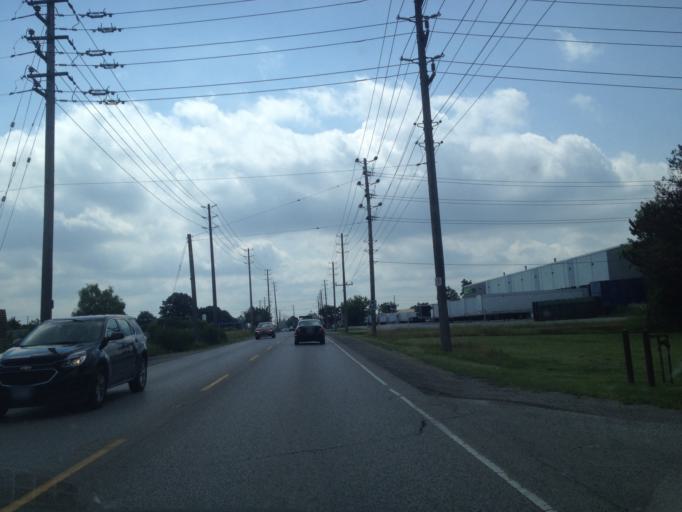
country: CA
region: Ontario
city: London
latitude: 43.0303
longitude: -81.1890
